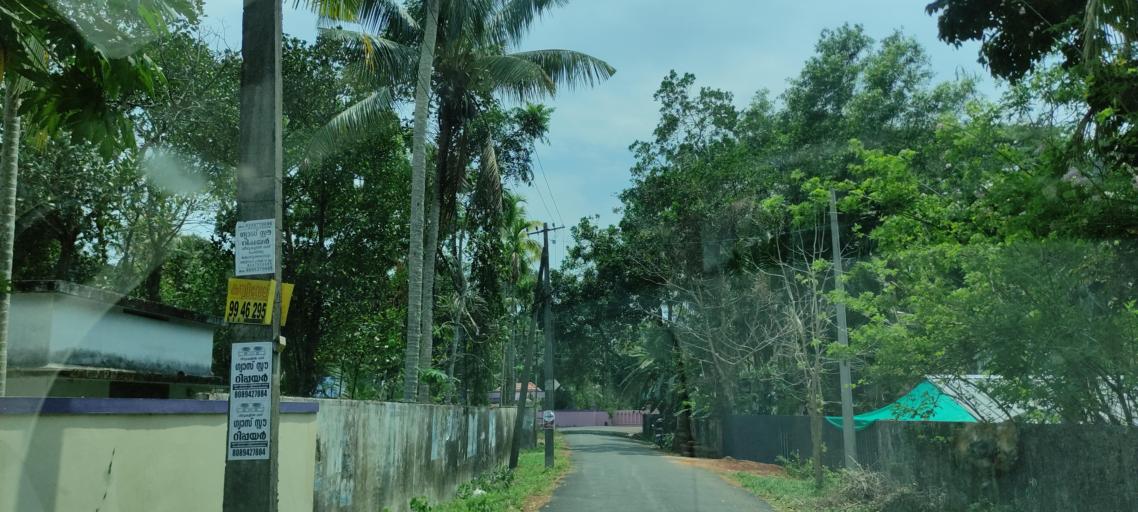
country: IN
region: Kerala
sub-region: Alappuzha
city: Vayalar
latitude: 9.7124
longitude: 76.3399
